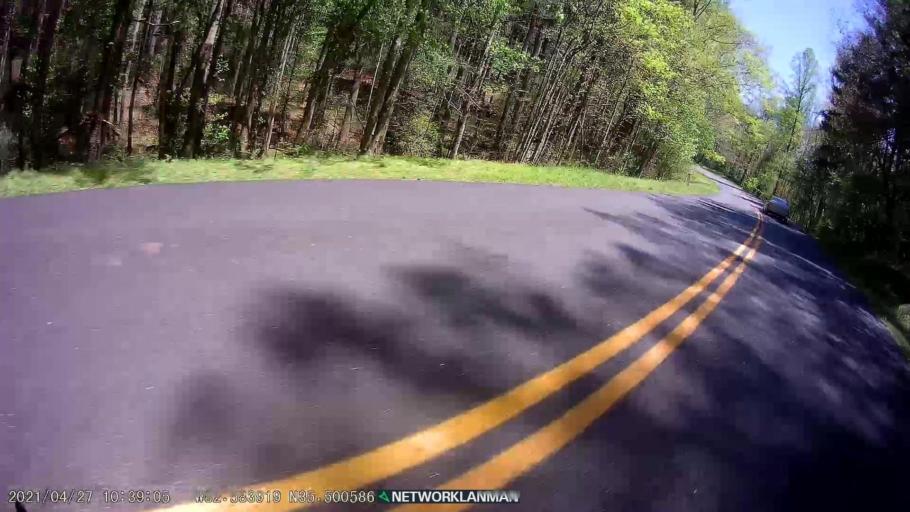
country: US
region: North Carolina
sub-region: Buncombe County
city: Bent Creek
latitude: 35.5004
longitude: -82.5837
